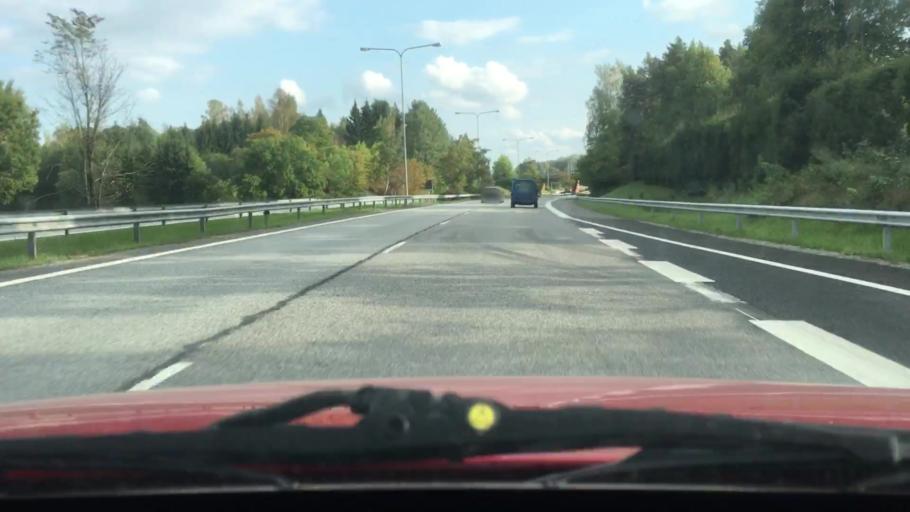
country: FI
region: Varsinais-Suomi
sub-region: Turku
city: Raisio
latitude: 60.4849
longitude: 22.1787
